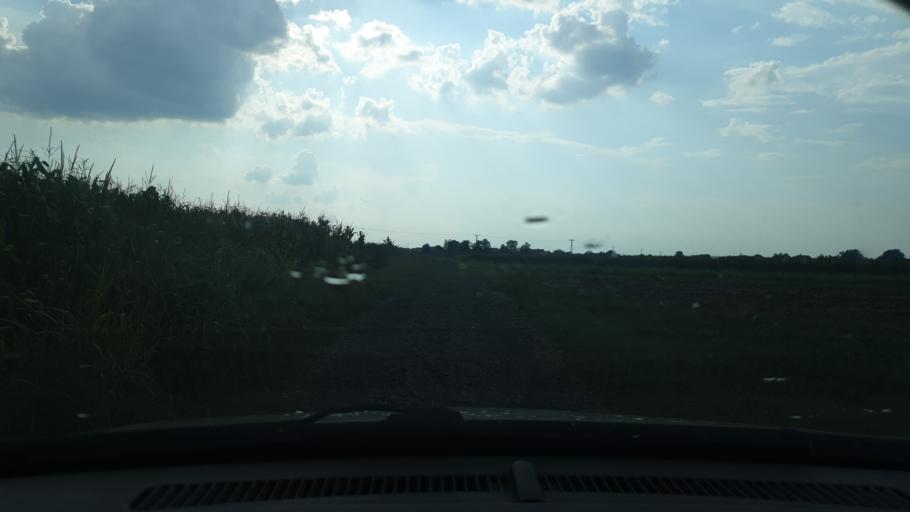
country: RS
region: Autonomna Pokrajina Vojvodina
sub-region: Sremski Okrug
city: Sremska Mitrovica
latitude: 44.9539
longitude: 19.6163
